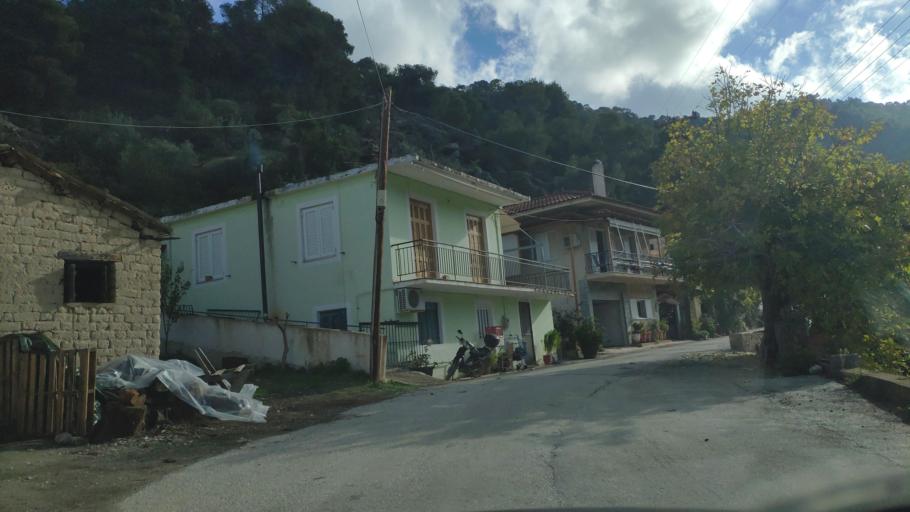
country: GR
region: West Greece
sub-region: Nomos Achaias
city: Aiyira
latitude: 38.1293
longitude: 22.4330
